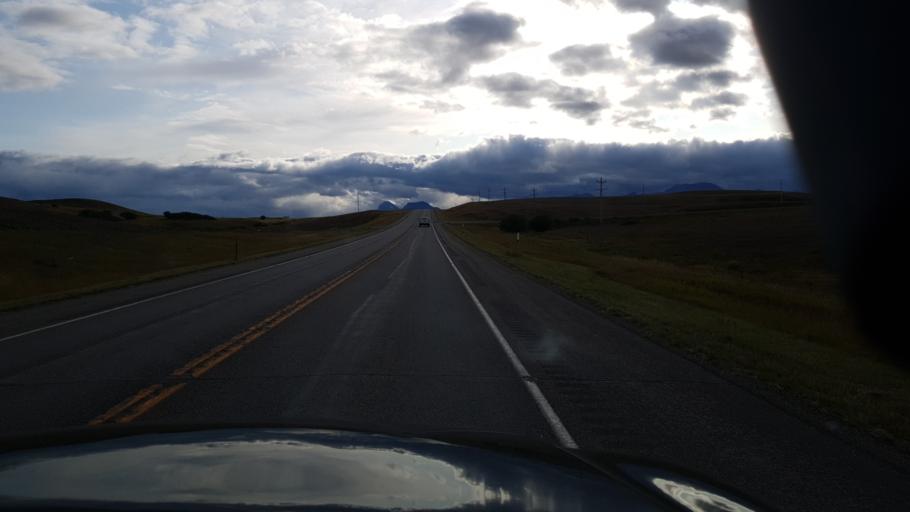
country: US
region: Montana
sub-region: Glacier County
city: South Browning
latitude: 48.5038
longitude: -113.1078
